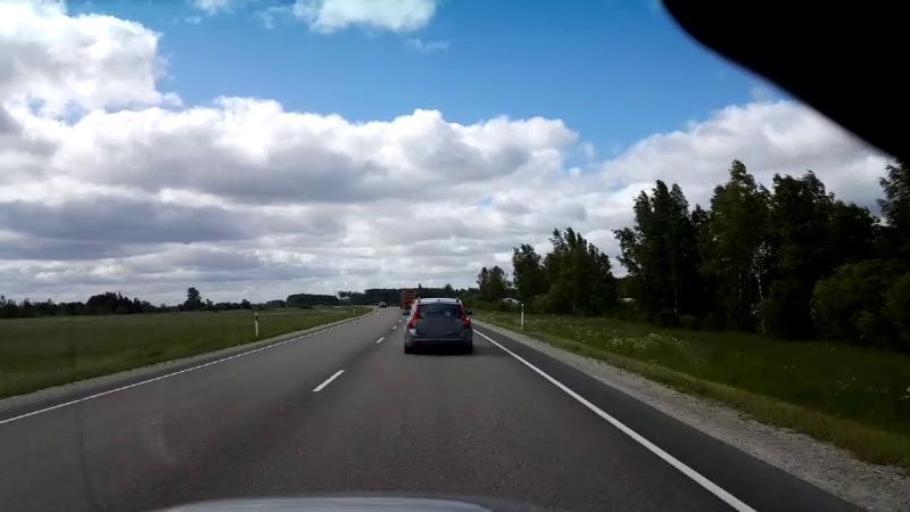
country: EE
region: Paernumaa
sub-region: Sauga vald
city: Sauga
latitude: 58.4857
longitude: 24.5280
